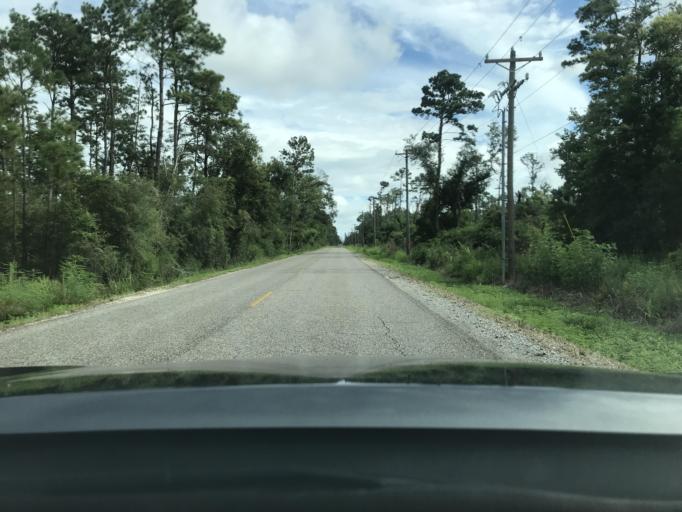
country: US
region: Louisiana
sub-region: Calcasieu Parish
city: Westlake
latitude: 30.2745
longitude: -93.2751
